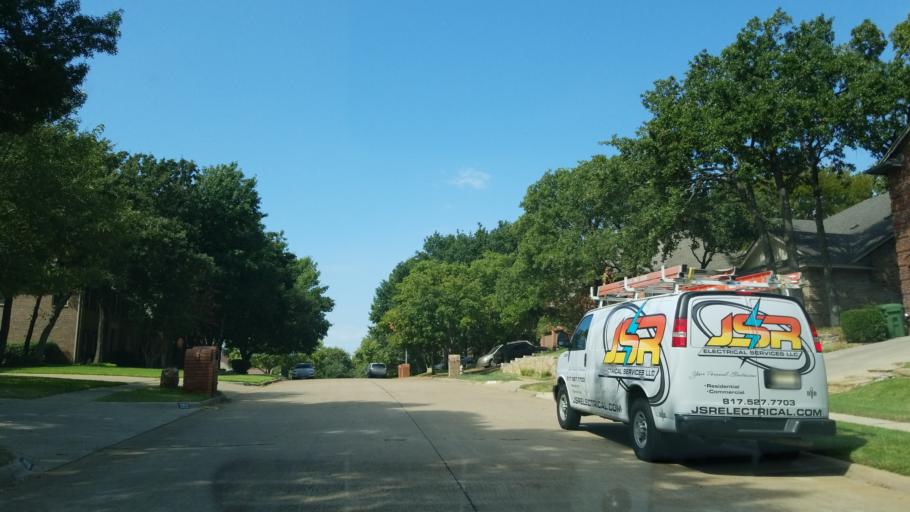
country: US
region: Texas
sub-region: Tarrant County
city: Grapevine
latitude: 32.8868
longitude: -97.0926
